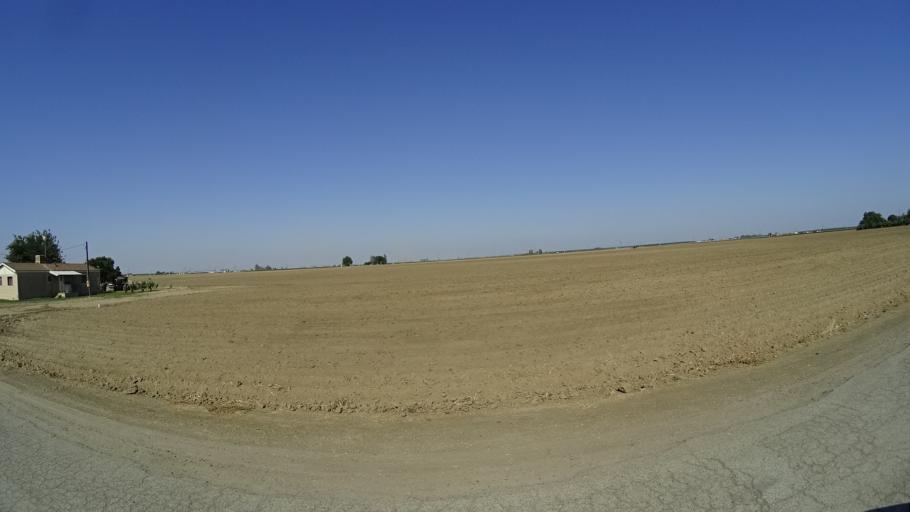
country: US
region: California
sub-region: Kings County
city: Home Garden
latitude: 36.2371
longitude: -119.5742
